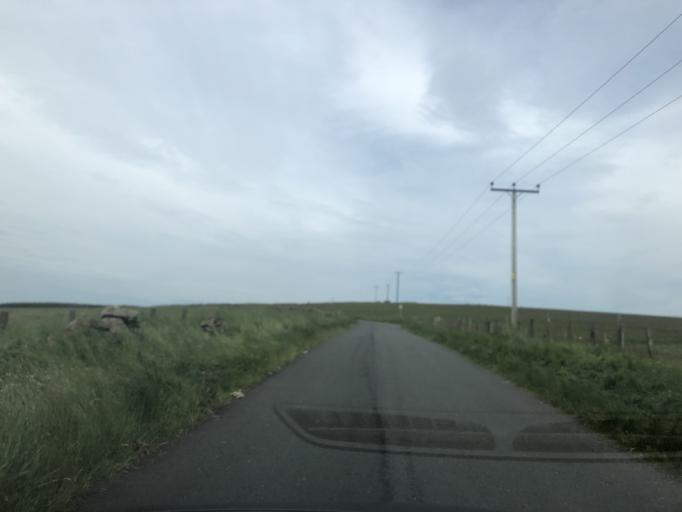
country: GB
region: Scotland
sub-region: The Scottish Borders
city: West Linton
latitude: 55.7649
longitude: -3.3249
